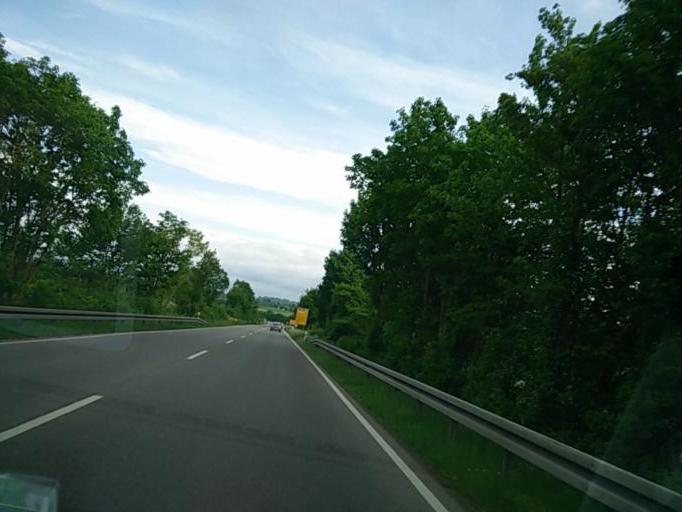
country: DE
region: Baden-Wuerttemberg
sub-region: Regierungsbezirk Stuttgart
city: Herrenberg
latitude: 48.5767
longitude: 8.9115
